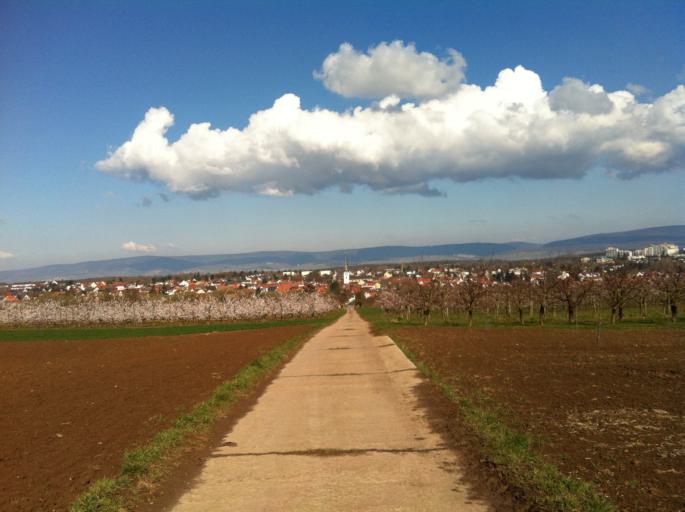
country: DE
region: Rheinland-Pfalz
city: Budenheim
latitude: 49.9806
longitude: 8.1820
